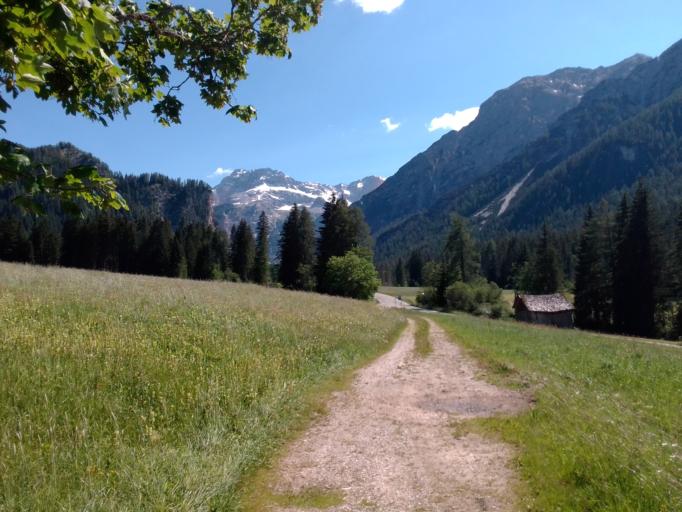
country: IT
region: Trentino-Alto Adige
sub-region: Bolzano
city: Braies
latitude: 46.7040
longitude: 12.1543
